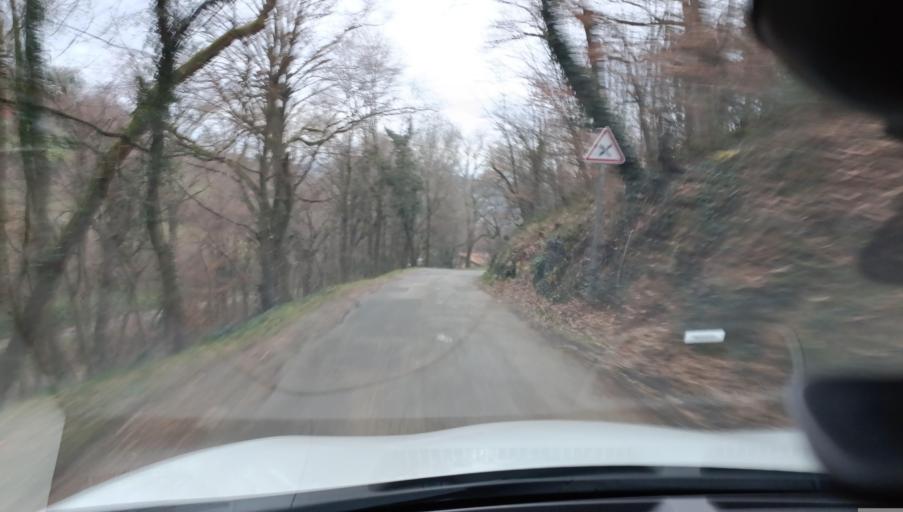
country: FR
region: Rhone-Alpes
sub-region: Departement de l'Isere
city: Chasse-sur-Rhone
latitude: 45.5750
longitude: 4.8207
